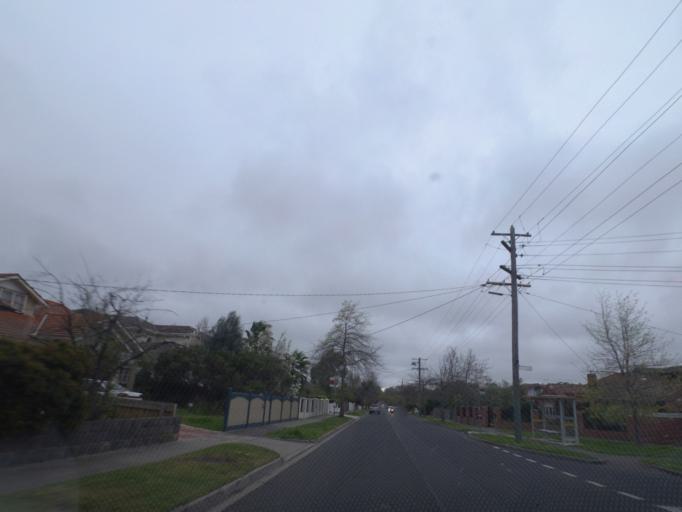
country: AU
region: Victoria
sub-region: Boroondara
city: Ashburton
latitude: -37.8684
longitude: 145.0693
